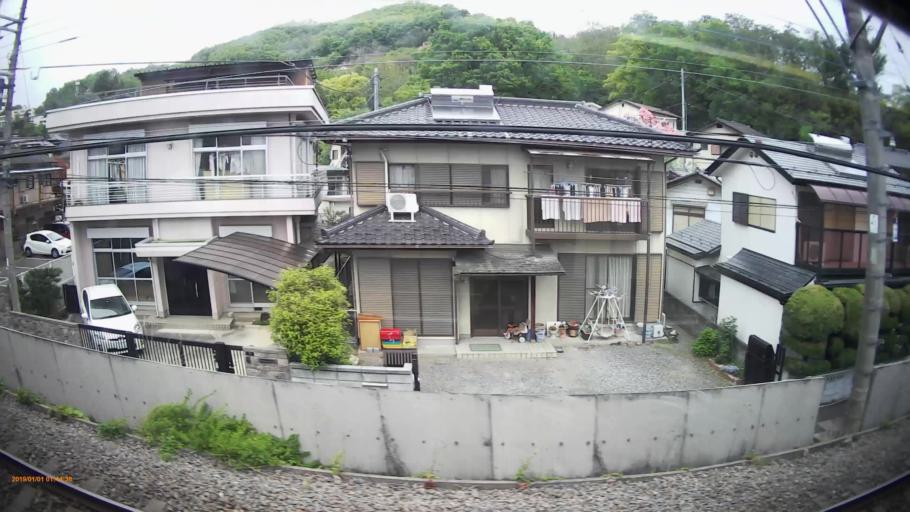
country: JP
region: Yamanashi
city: Kofu-shi
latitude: 35.6639
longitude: 138.5772
